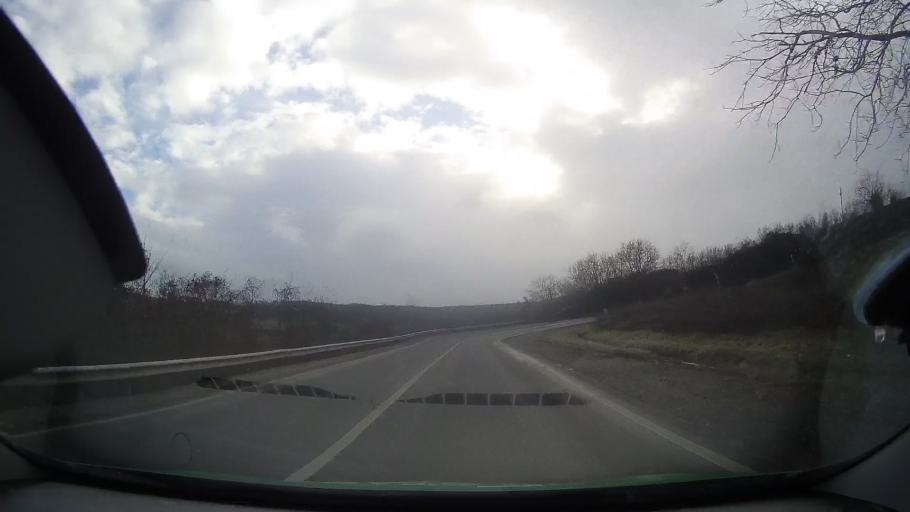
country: RO
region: Mures
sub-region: Municipiul Tarnaveni
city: Tarnaveni
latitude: 46.3588
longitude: 24.2715
